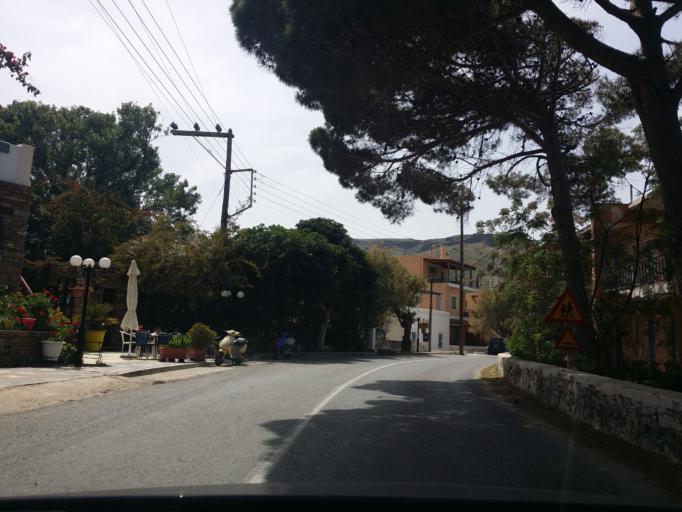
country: GR
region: South Aegean
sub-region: Nomos Kykladon
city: Kea
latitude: 37.6575
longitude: 24.3154
